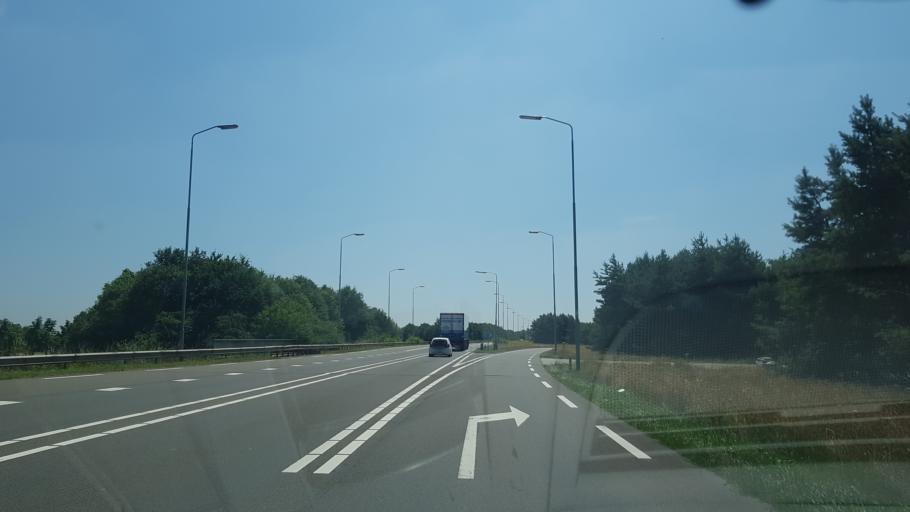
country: NL
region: North Brabant
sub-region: Gemeente Helmond
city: Helmond
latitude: 51.4765
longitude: 5.7157
